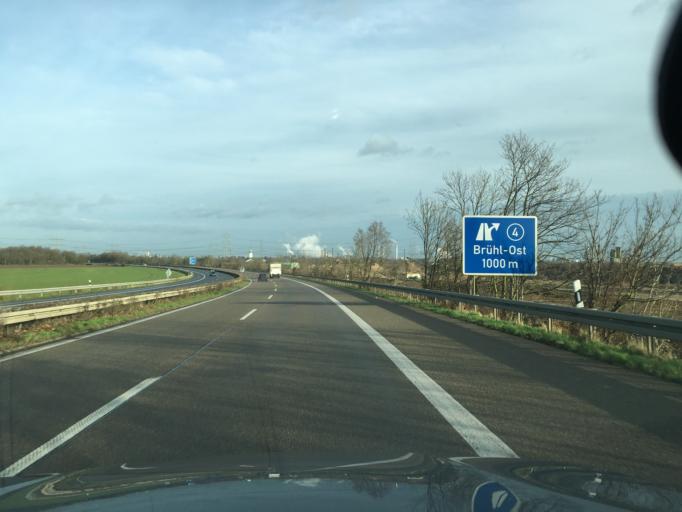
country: DE
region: North Rhine-Westphalia
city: Bruhl
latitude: 50.8173
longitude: 6.9308
